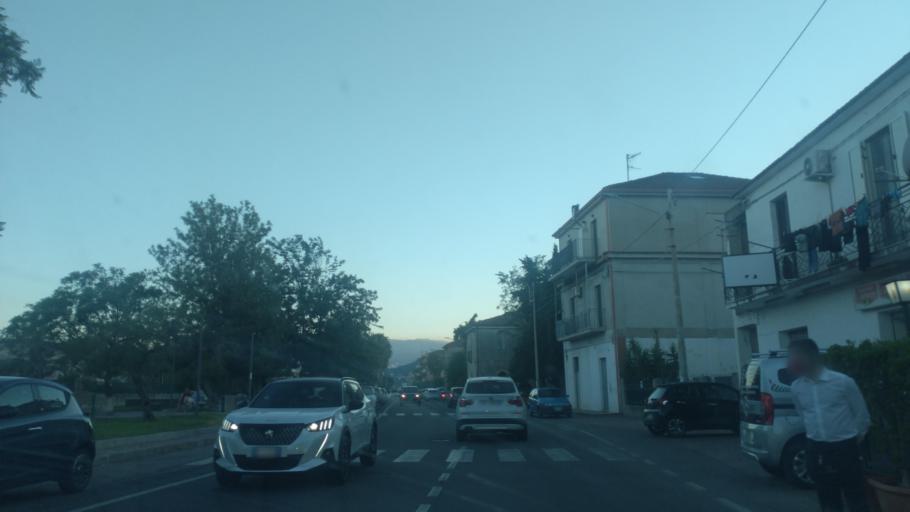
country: IT
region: Calabria
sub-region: Provincia di Catanzaro
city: Montepaone Lido
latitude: 38.7297
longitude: 16.5426
